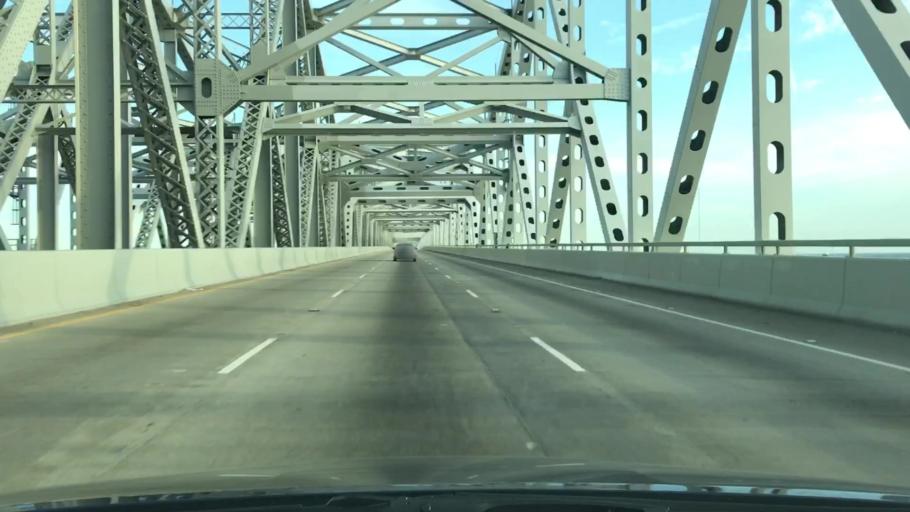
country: US
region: Louisiana
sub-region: Jefferson Parish
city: Bridge City
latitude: 29.9455
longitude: -90.1707
